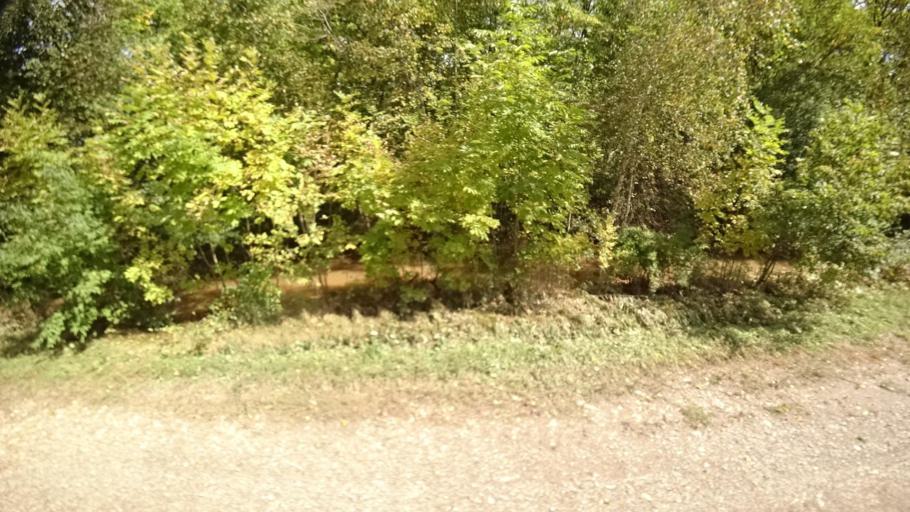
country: RU
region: Primorskiy
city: Yakovlevka
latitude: 44.6645
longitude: 133.7508
